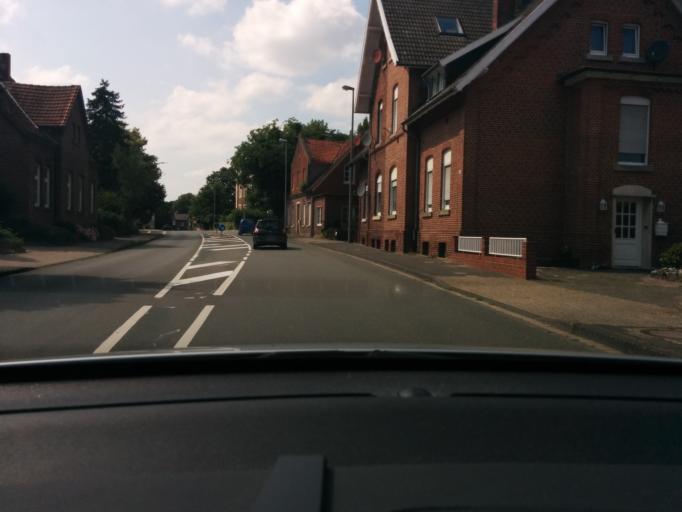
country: DE
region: North Rhine-Westphalia
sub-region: Regierungsbezirk Munster
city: Ochtrup
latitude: 52.1970
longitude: 7.2395
